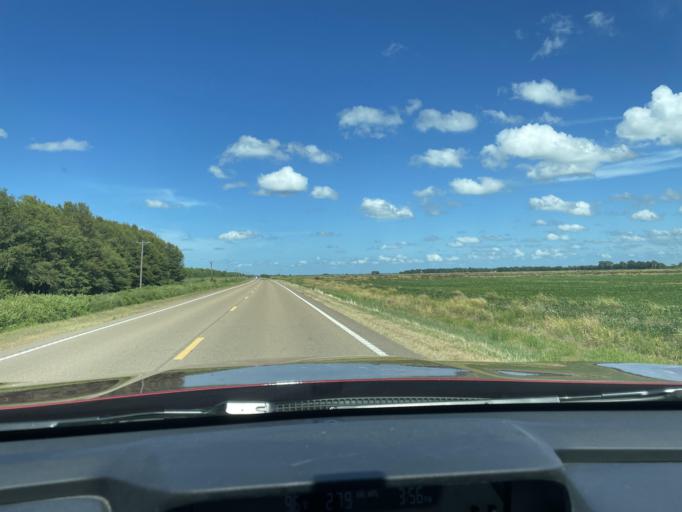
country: US
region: Mississippi
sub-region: Humphreys County
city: Belzoni
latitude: 33.1826
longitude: -90.6262
